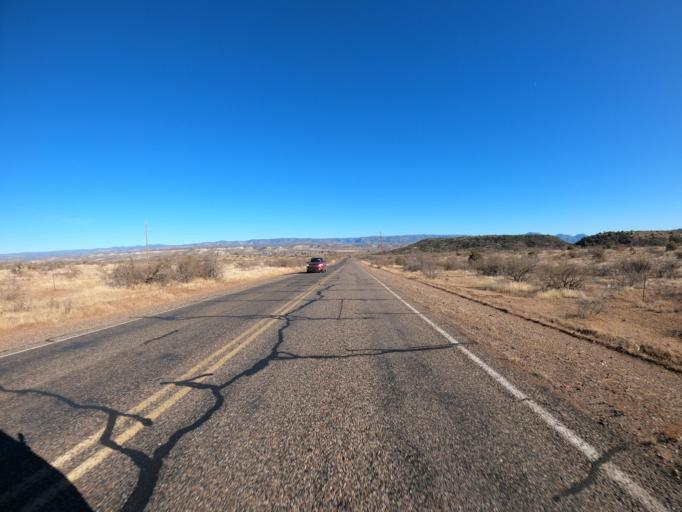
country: US
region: Arizona
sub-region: Yavapai County
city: Camp Verde
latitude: 34.5581
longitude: -111.8950
